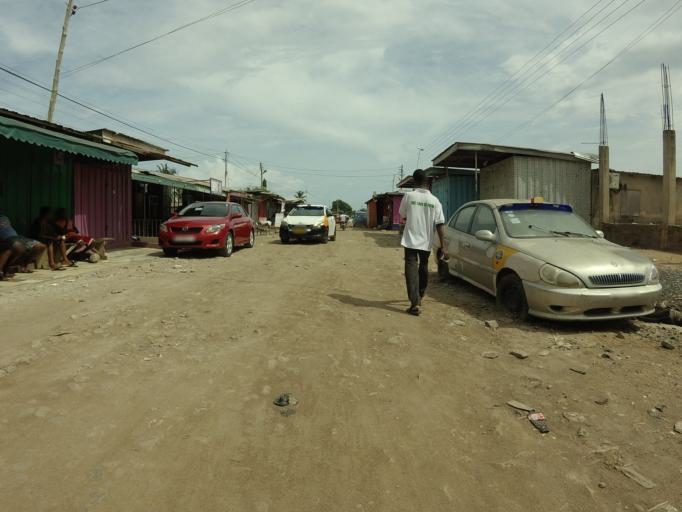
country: GH
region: Greater Accra
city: Accra
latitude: 5.5972
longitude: -0.2127
